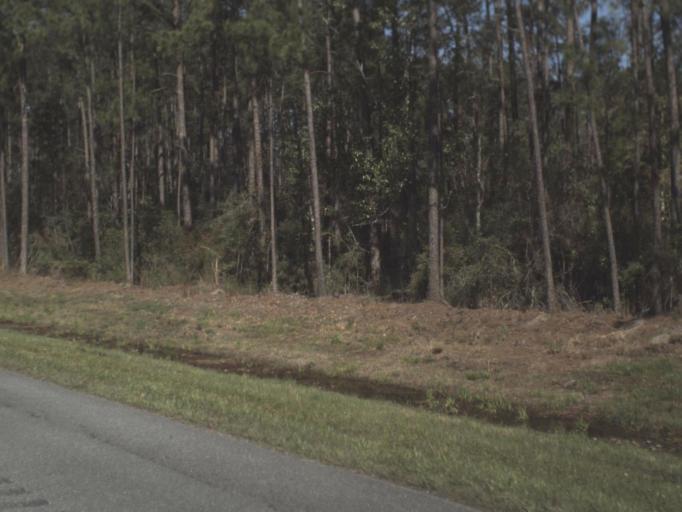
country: US
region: Florida
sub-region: Walton County
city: DeFuniak Springs
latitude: 30.6907
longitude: -86.0347
